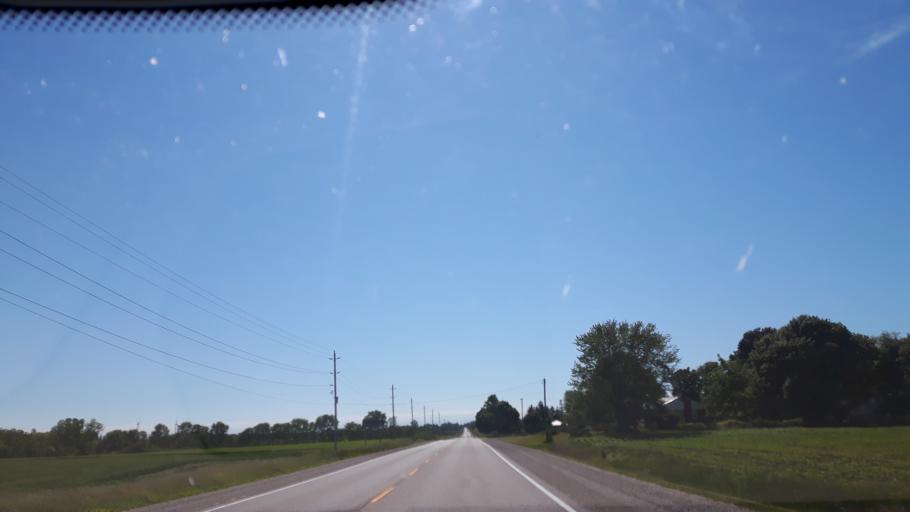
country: CA
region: Ontario
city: Bluewater
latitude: 43.4185
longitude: -81.6510
